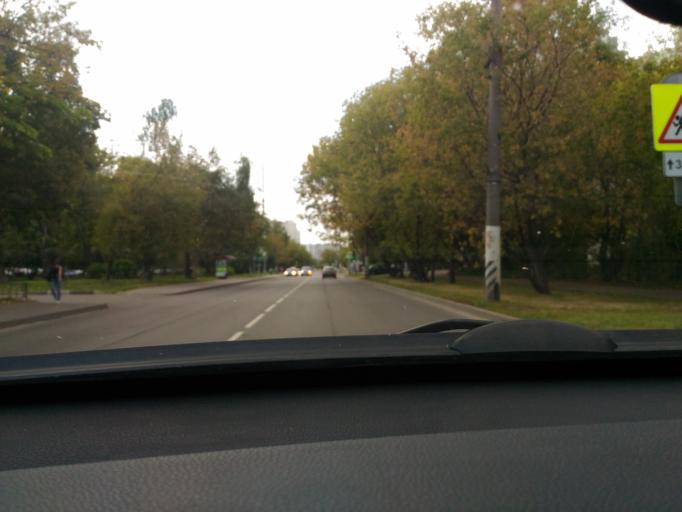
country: RU
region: Moscow
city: Vatutino
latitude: 55.8820
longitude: 37.6933
